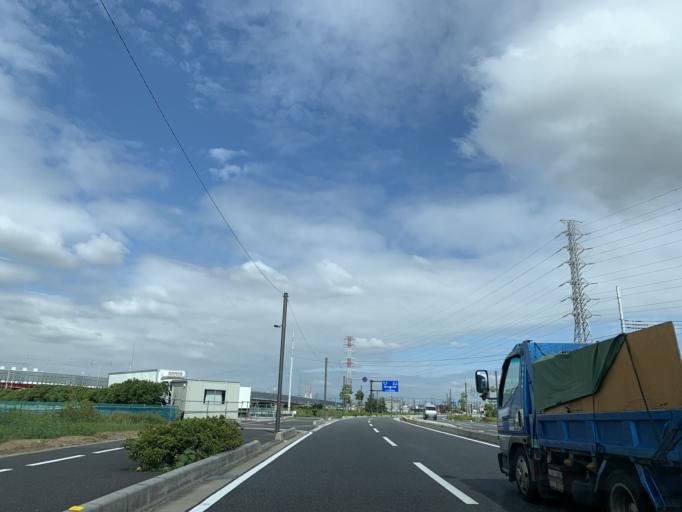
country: JP
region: Chiba
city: Nagareyama
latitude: 35.8431
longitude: 139.8731
